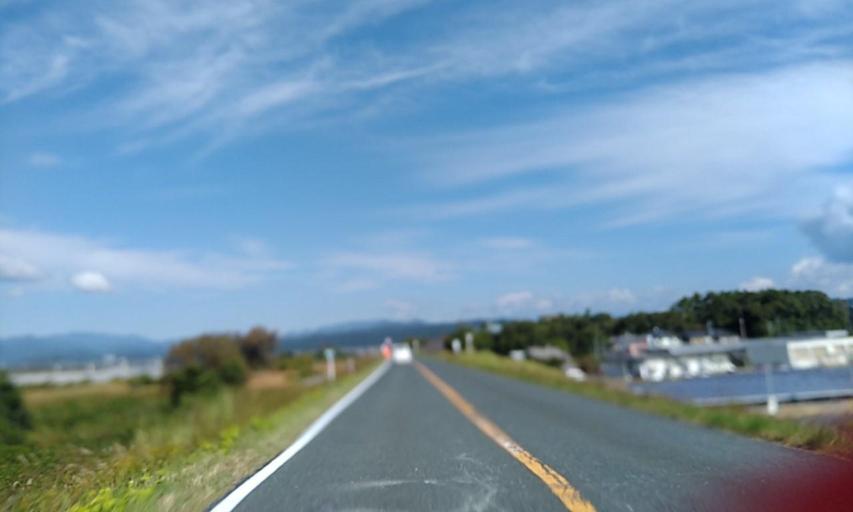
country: JP
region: Shizuoka
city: Hamakita
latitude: 34.8154
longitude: 137.8310
